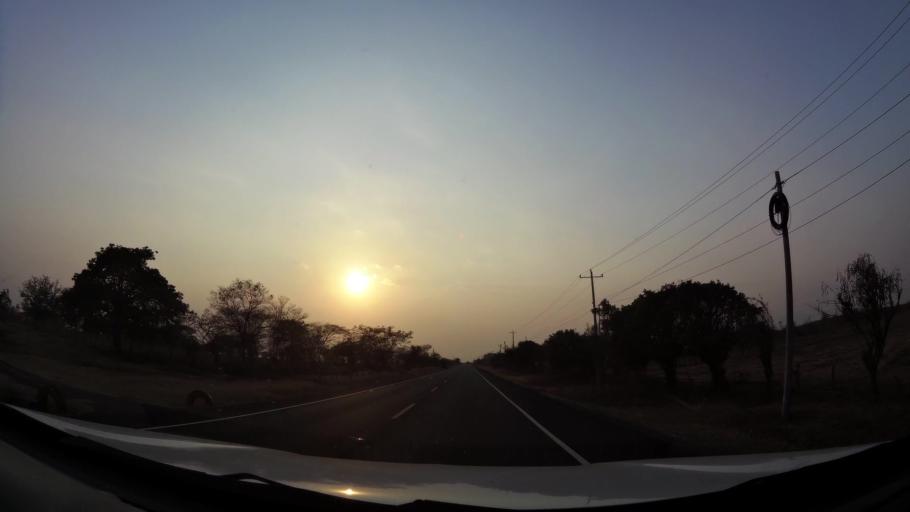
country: NI
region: Leon
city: La Paz Centro
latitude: 12.3223
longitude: -86.6203
